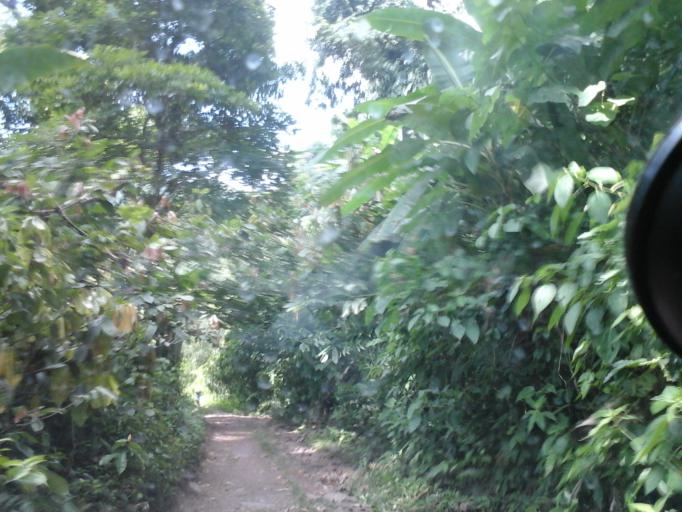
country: CO
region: Cesar
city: Manaure Balcon del Cesar
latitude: 10.2933
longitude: -73.0760
